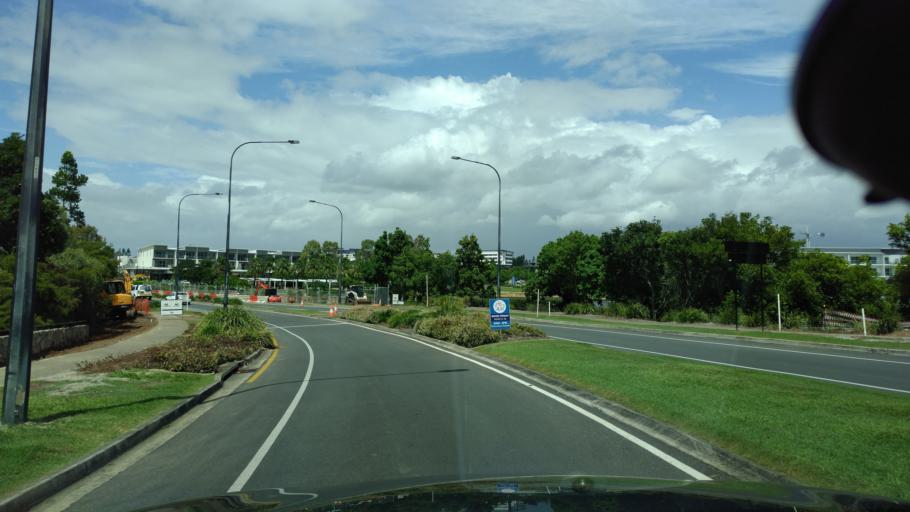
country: AU
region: Queensland
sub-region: Moreton Bay
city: Mango Hill
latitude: -27.2349
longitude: 153.0213
